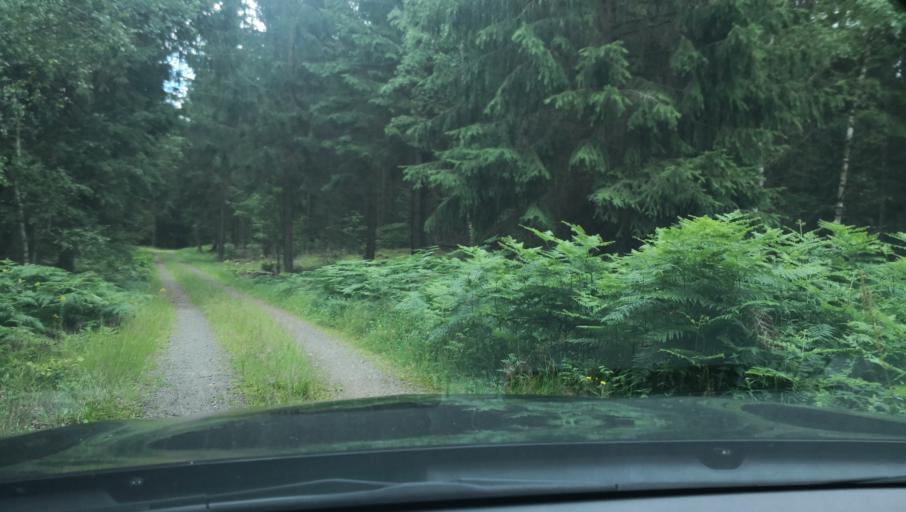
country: SE
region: Skane
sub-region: Simrishamns Kommun
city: Kivik
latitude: 55.6125
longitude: 14.1179
